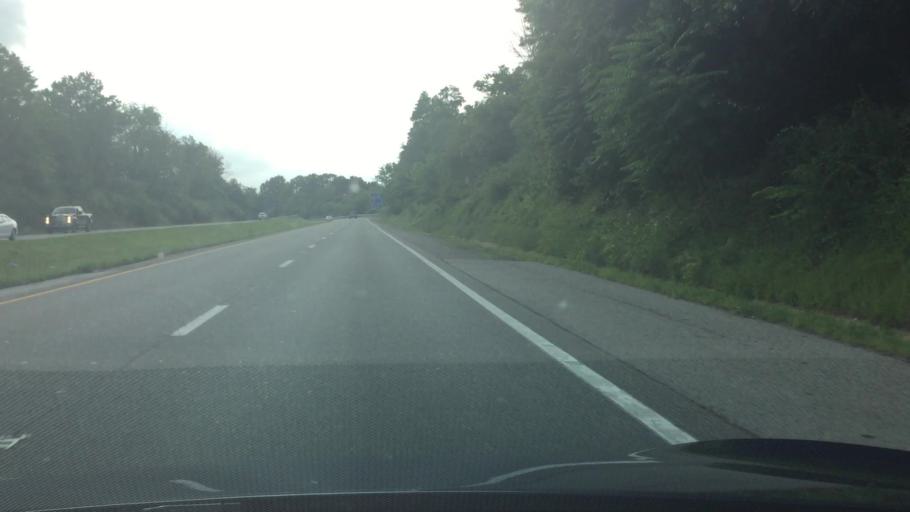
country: US
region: Virginia
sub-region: Montgomery County
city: Christiansburg
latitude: 37.1502
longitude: -80.3993
